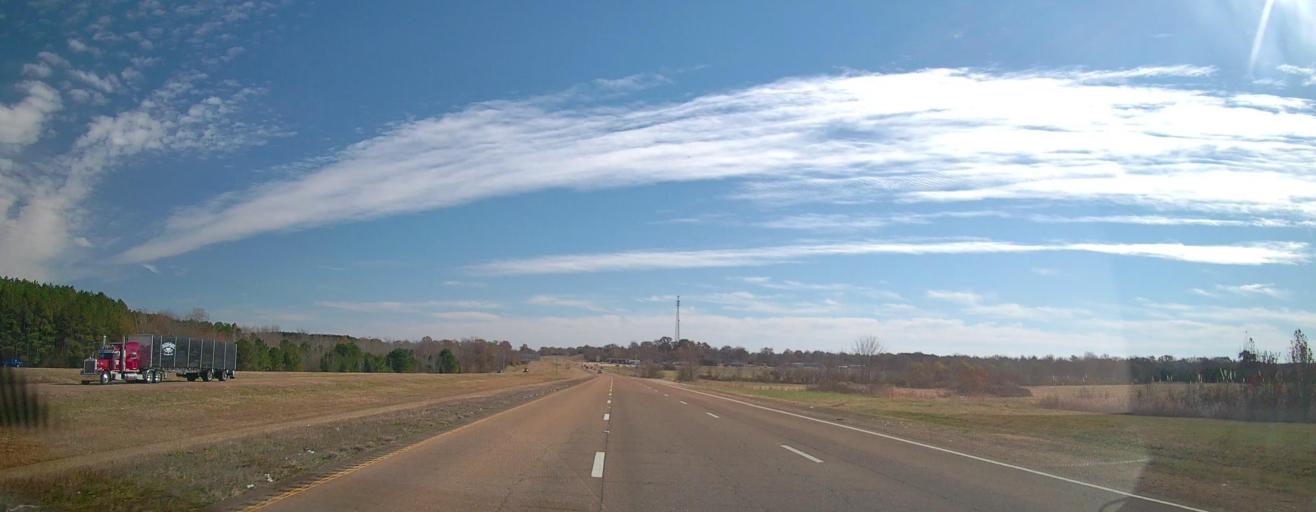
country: US
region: Tennessee
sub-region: Fayette County
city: Piperton
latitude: 34.9631
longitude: -89.5373
